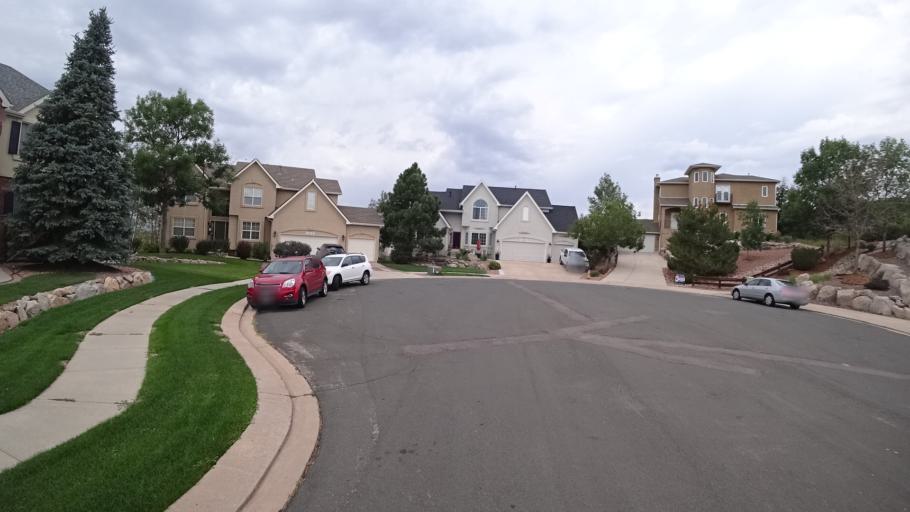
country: US
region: Colorado
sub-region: El Paso County
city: Gleneagle
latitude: 39.0053
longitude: -104.8021
